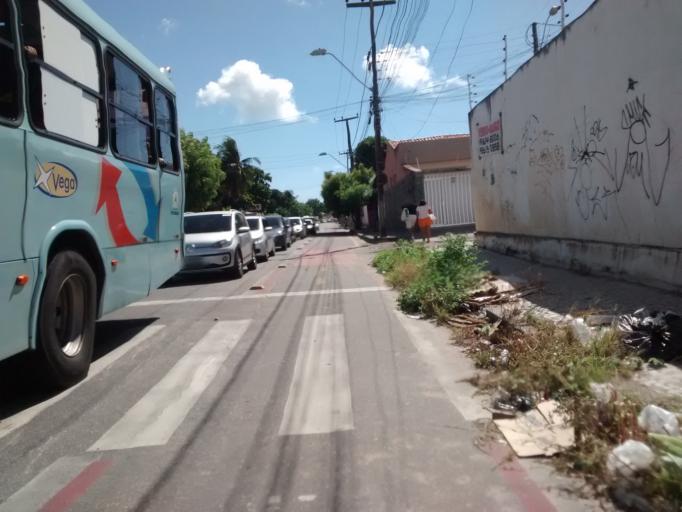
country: BR
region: Ceara
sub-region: Fortaleza
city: Fortaleza
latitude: -3.7240
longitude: -38.5508
